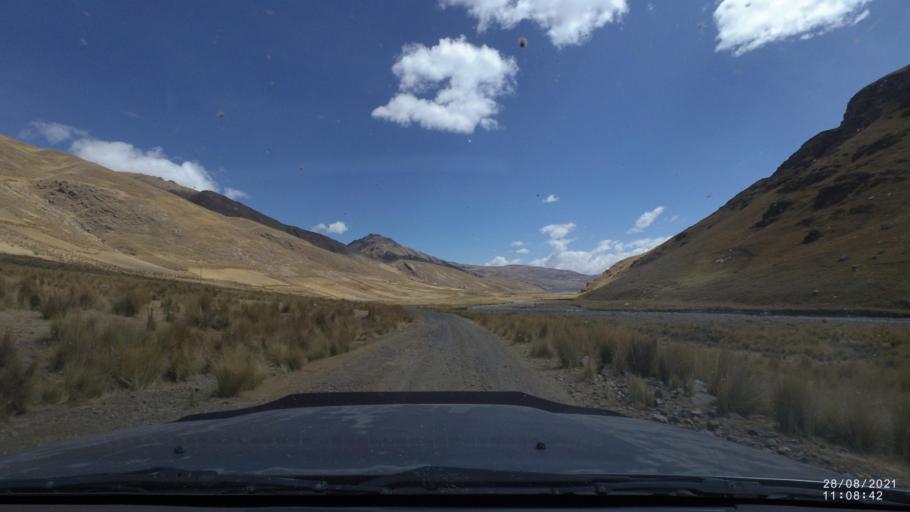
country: BO
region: Cochabamba
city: Cochabamba
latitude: -17.1652
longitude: -66.3040
